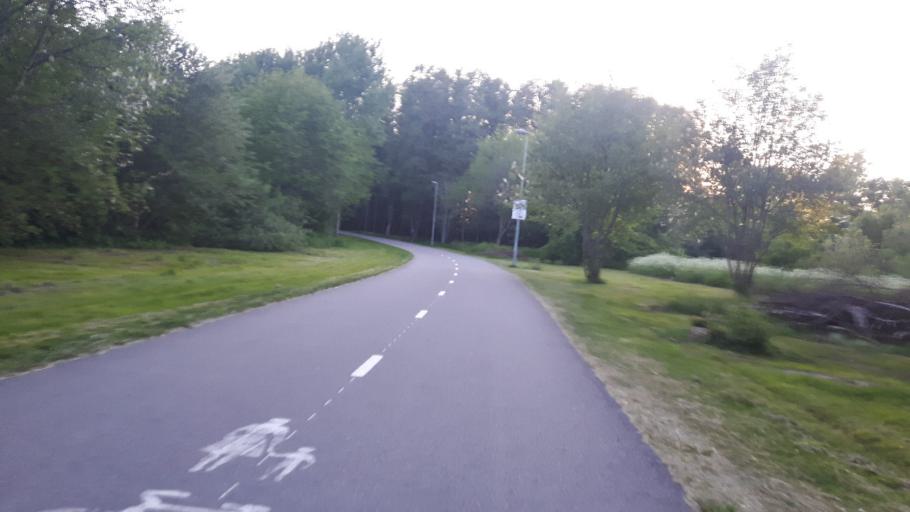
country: EE
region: Paernumaa
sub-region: Paernu linn
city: Parnu
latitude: 58.3705
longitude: 24.5298
